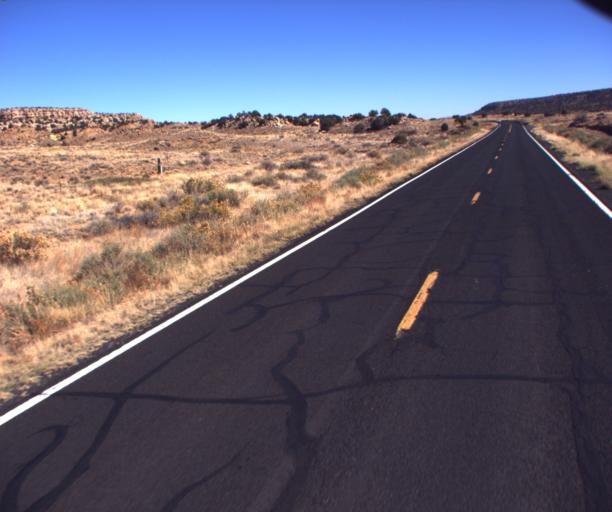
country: US
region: Arizona
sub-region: Navajo County
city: First Mesa
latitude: 35.8298
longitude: -110.2799
